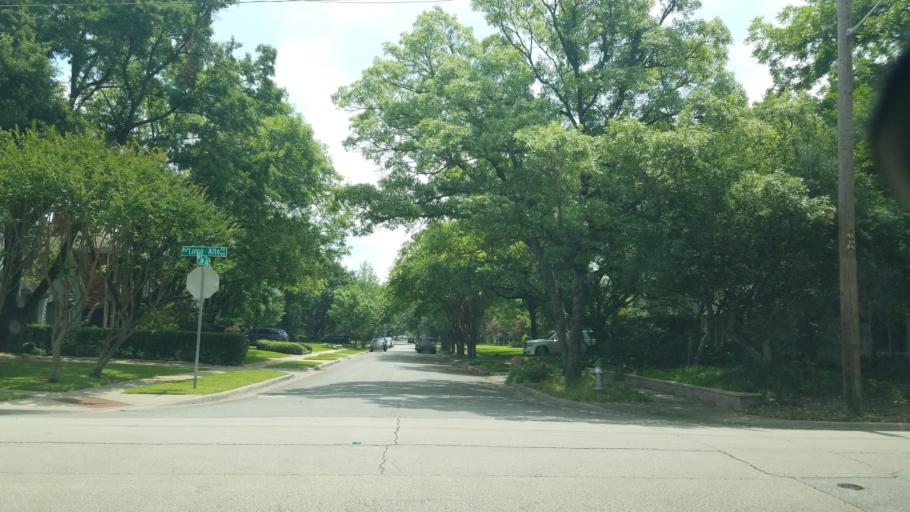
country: US
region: Texas
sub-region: Dallas County
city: University Park
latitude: 32.8388
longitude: -96.8131
